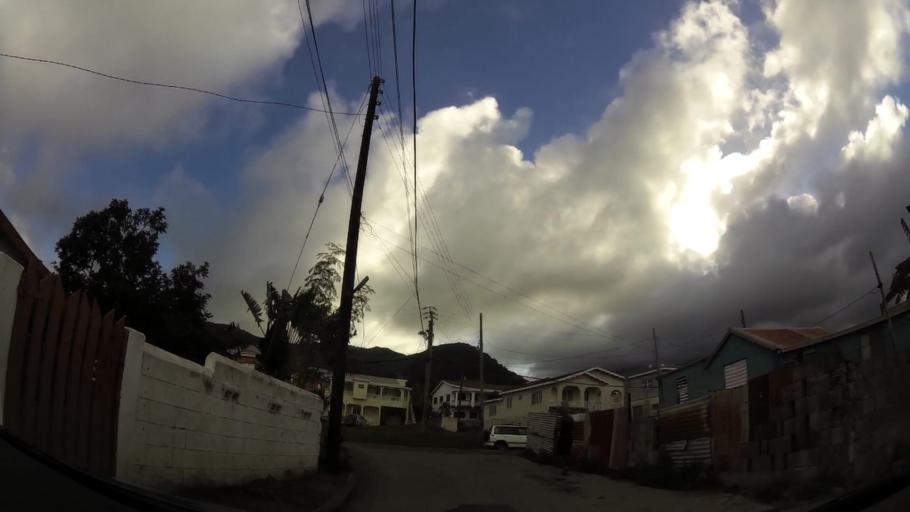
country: KN
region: Saint Mary Cayon
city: Cayon
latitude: 17.3493
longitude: -62.7290
